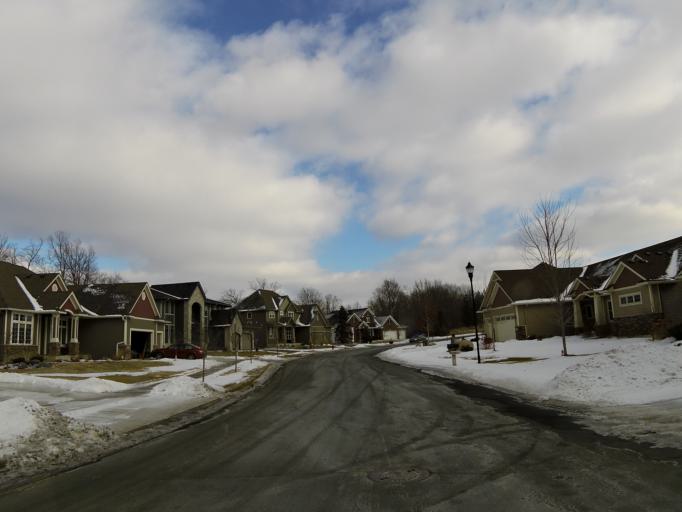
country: US
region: Minnesota
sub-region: Scott County
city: Prior Lake
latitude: 44.7370
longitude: -93.4495
